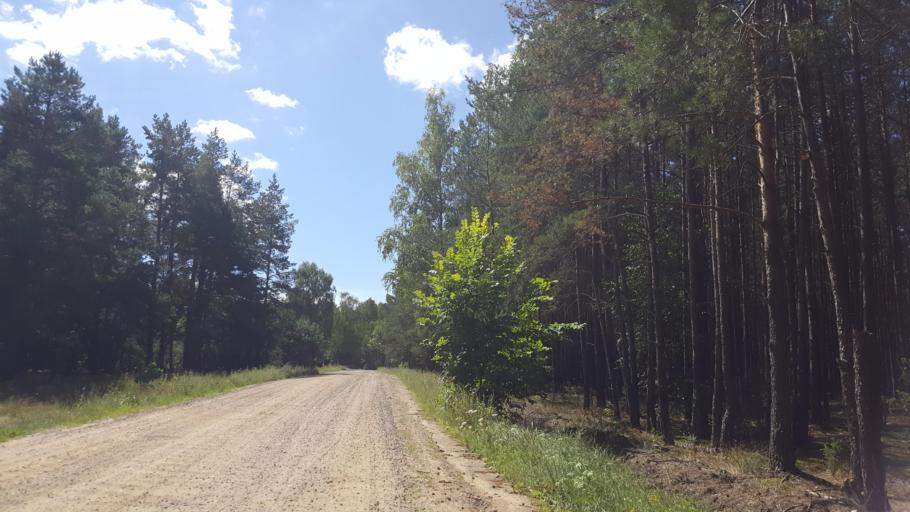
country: BY
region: Brest
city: Zhabinka
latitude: 52.3993
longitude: 24.0895
